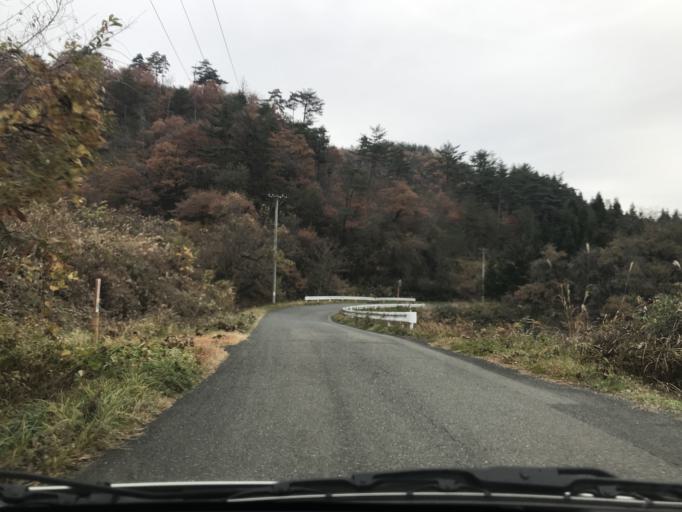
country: JP
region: Iwate
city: Ichinoseki
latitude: 39.0115
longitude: 141.0659
